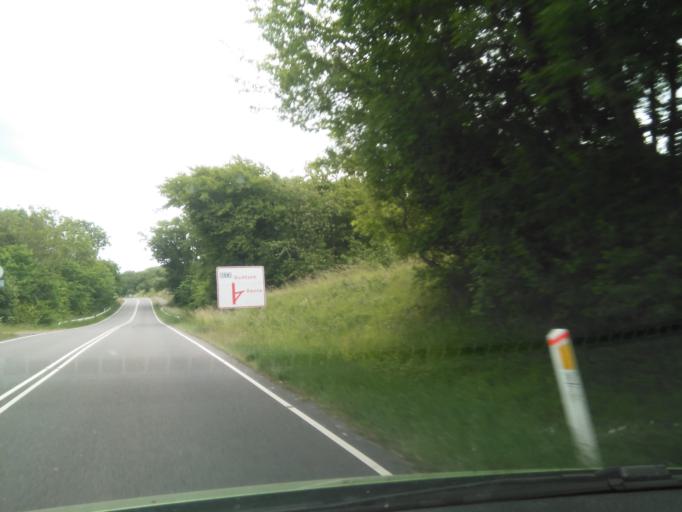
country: DK
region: Capital Region
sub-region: Bornholm Kommune
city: Akirkeby
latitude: 55.2247
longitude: 14.8897
